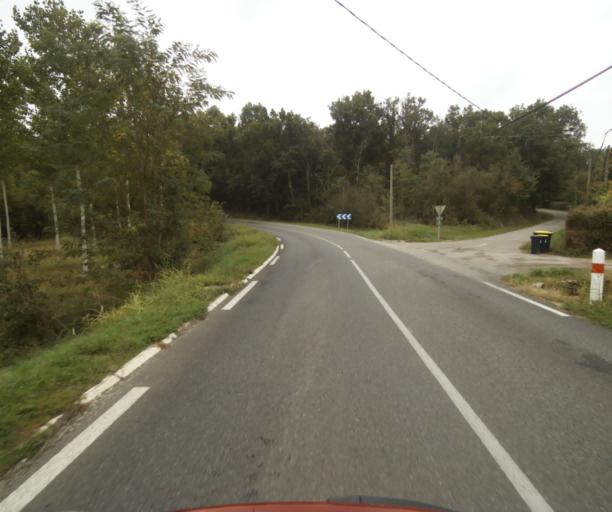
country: FR
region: Midi-Pyrenees
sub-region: Departement du Tarn-et-Garonne
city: Verdun-sur-Garonne
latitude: 43.7966
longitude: 1.2254
